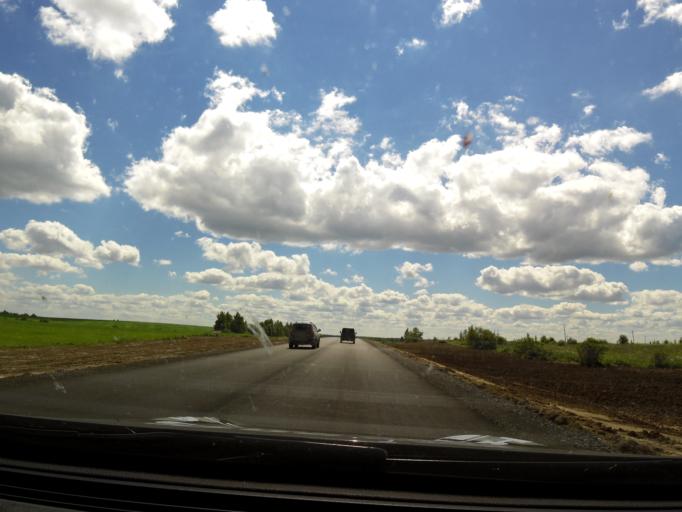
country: RU
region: Vologda
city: Molochnoye
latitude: 59.3049
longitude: 39.6866
